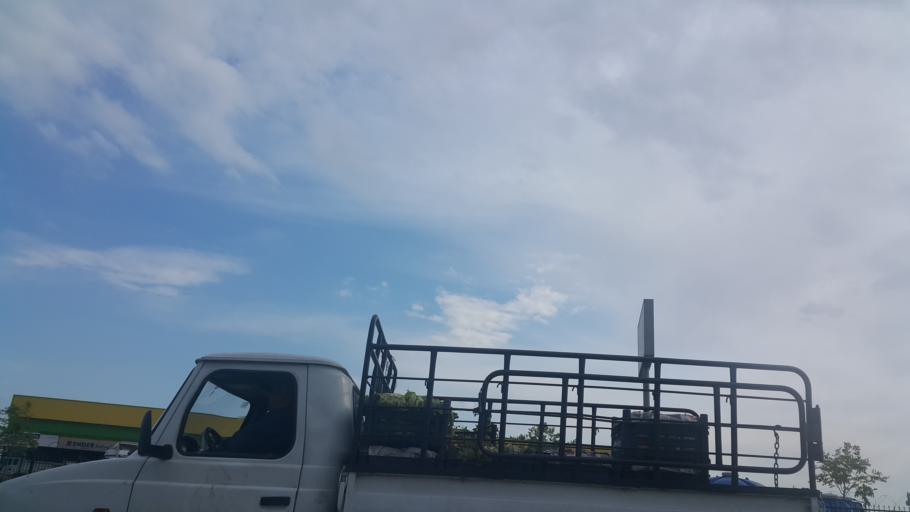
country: TR
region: Adana
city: Seyhan
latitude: 36.9962
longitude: 35.2597
